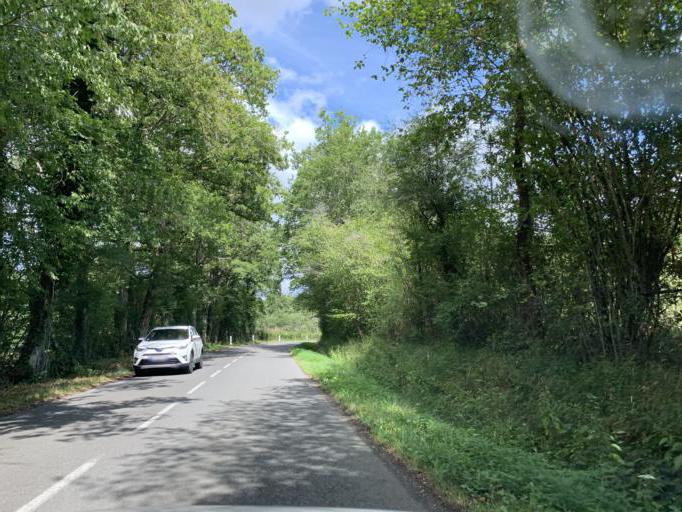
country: FR
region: Bourgogne
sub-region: Departement de la Nievre
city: Saint-Amand-en-Puisaye
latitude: 47.5859
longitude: 3.1620
